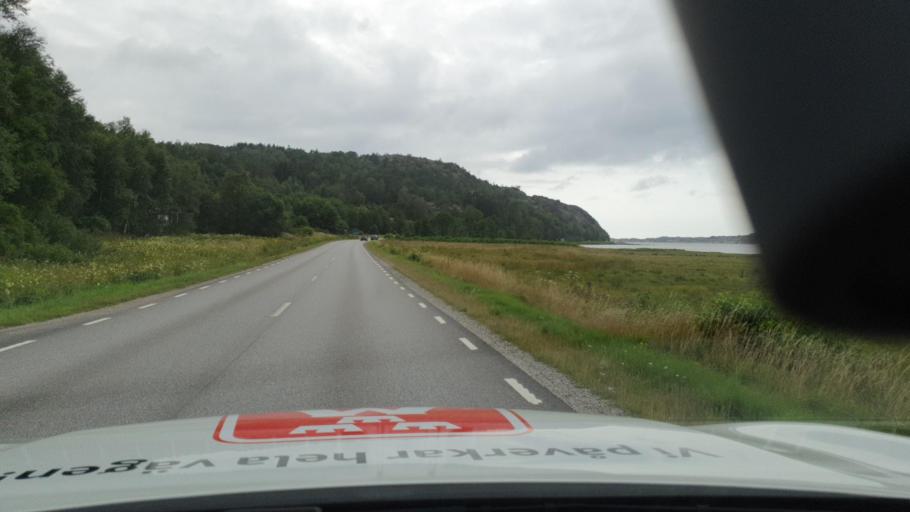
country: SE
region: Vaestra Goetaland
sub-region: Sotenas Kommun
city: Hunnebostrand
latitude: 58.4866
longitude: 11.3598
